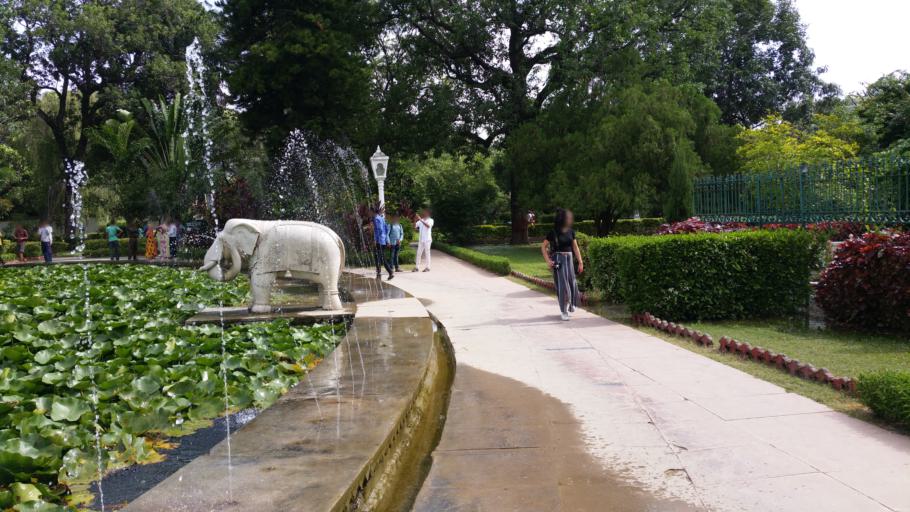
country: IN
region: Rajasthan
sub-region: Udaipur
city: Udaipur
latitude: 24.6032
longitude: 73.6844
